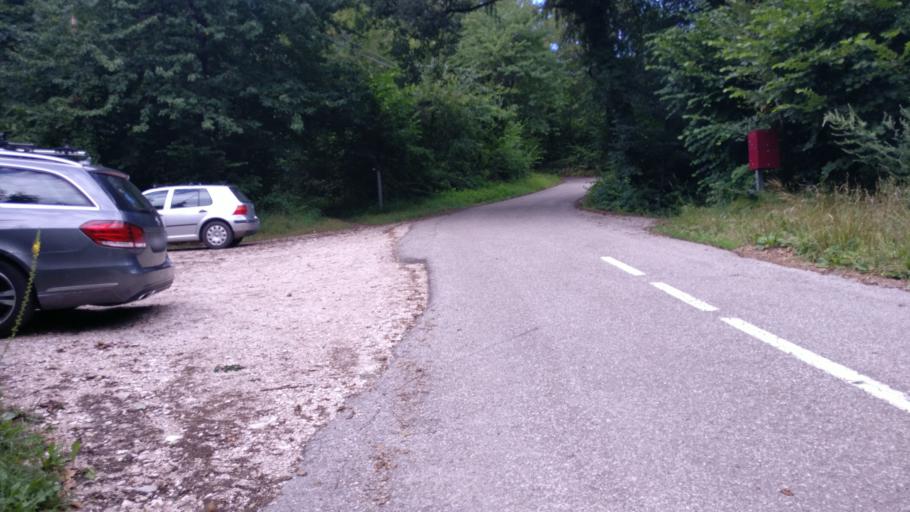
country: IT
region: Trentino-Alto Adige
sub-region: Bolzano
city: San Paolo
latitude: 46.4718
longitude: 11.2420
